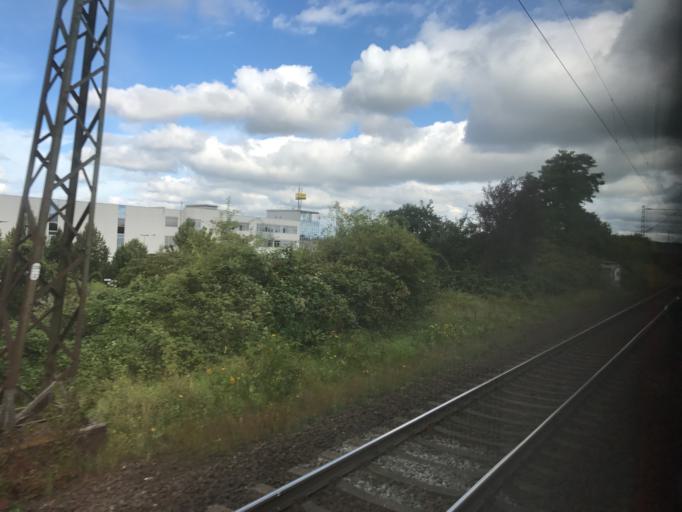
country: DE
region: Hesse
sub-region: Regierungsbezirk Giessen
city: Langgons
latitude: 50.5330
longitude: 8.6608
